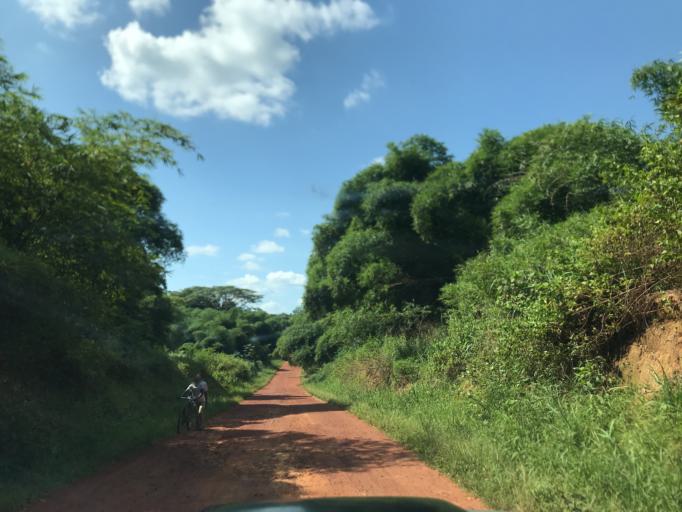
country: CD
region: Eastern Province
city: Kisangani
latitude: 1.2448
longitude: 25.2727
